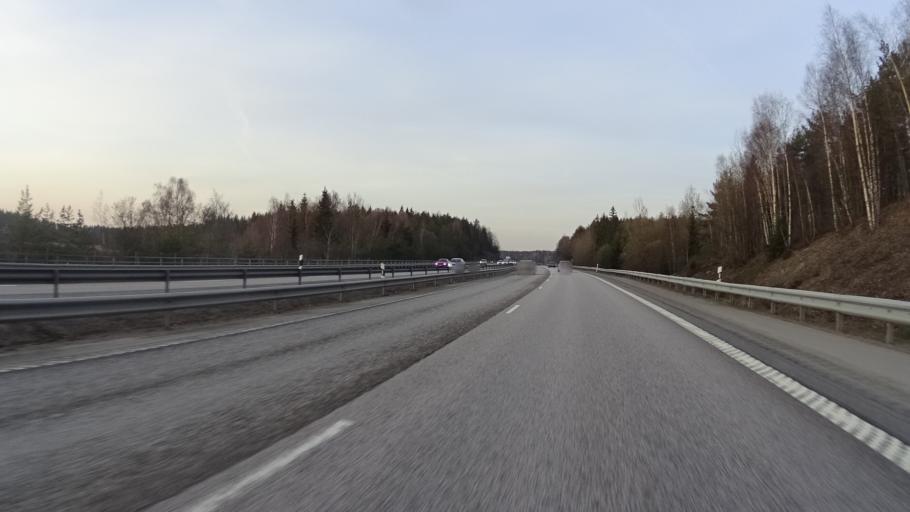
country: SE
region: Stockholm
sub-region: Sodertalje Kommun
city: Pershagen
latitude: 59.1255
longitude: 17.6330
